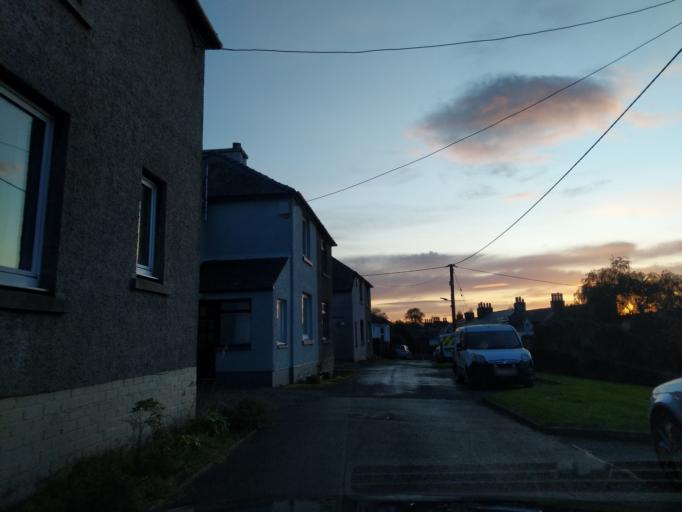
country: GB
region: Scotland
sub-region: Dumfries and Galloway
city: Kirkcudbright
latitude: 54.8352
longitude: -4.0493
